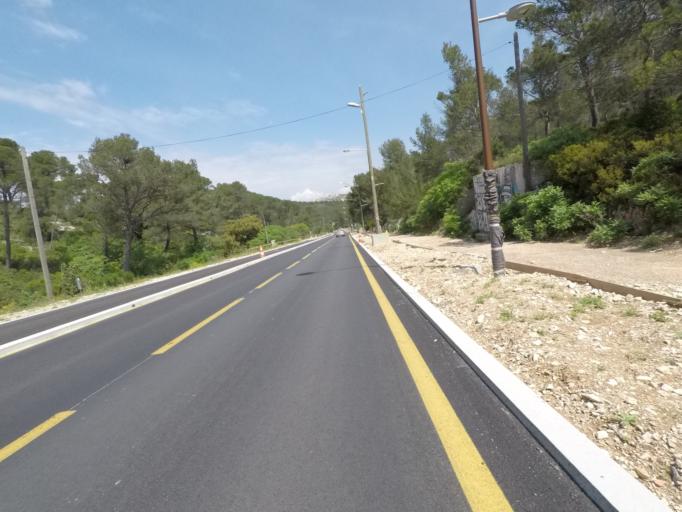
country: FR
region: Provence-Alpes-Cote d'Azur
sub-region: Departement des Bouches-du-Rhone
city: Marseille 09
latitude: 43.2361
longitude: 5.4360
